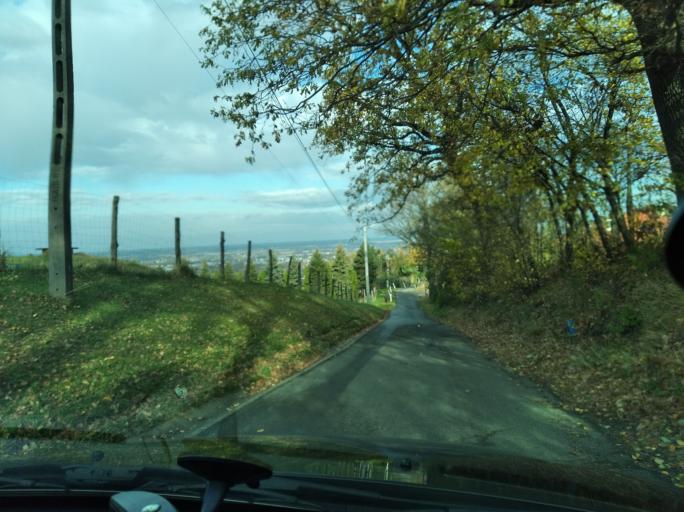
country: PL
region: Subcarpathian Voivodeship
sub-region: Powiat debicki
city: Debica
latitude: 50.0360
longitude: 21.4510
